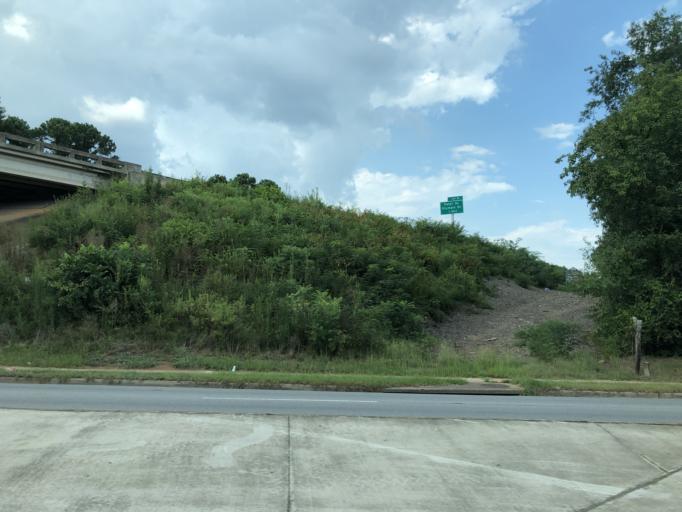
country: US
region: Georgia
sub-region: Clarke County
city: Athens
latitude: 33.9465
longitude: -83.3555
